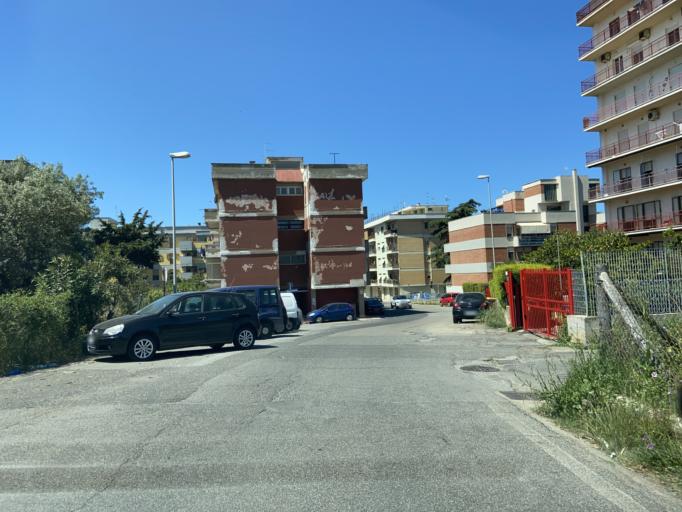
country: IT
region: Latium
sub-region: Citta metropolitana di Roma Capitale
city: Civitavecchia
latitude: 42.0841
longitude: 11.8156
